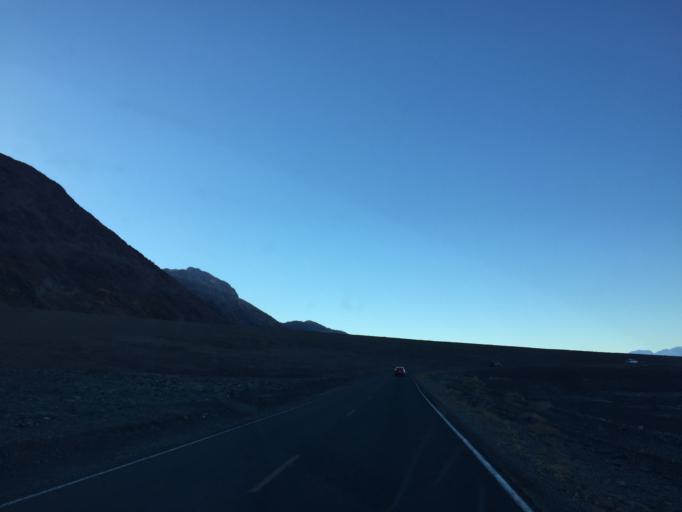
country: US
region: Nevada
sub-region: Nye County
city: Beatty
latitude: 36.2150
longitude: -116.7734
